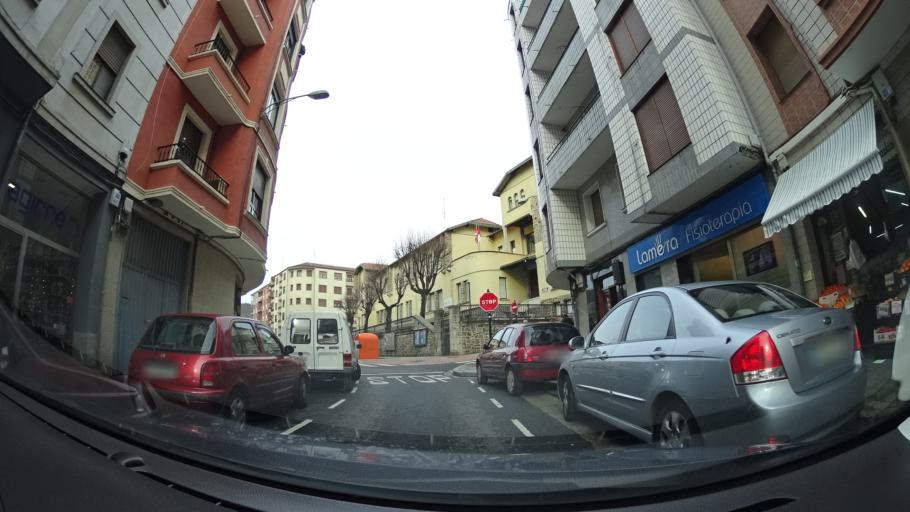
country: ES
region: Basque Country
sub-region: Bizkaia
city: Bermeo
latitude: 43.4207
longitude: -2.7256
